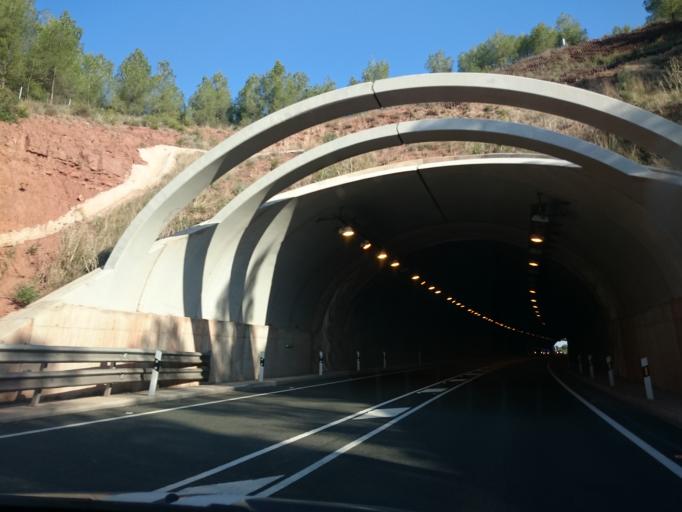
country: ES
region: Catalonia
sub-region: Provincia de Barcelona
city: Sant Salvador de Guardiola
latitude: 41.7051
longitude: 1.7800
